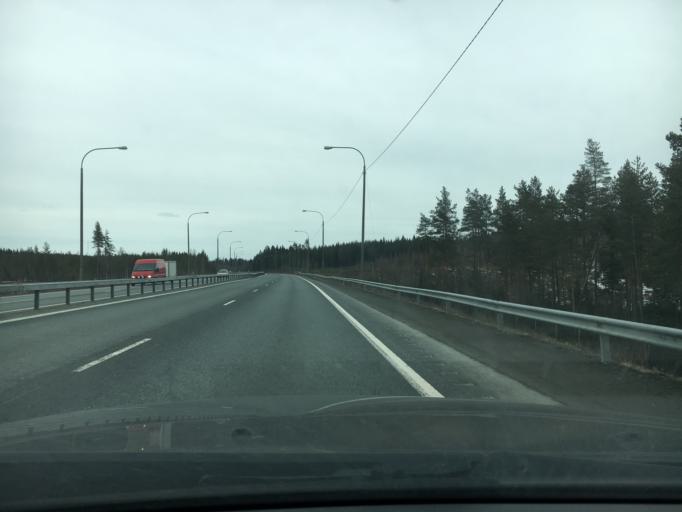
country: FI
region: Northern Savo
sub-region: Kuopio
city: Kuopio
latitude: 62.7348
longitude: 27.5873
